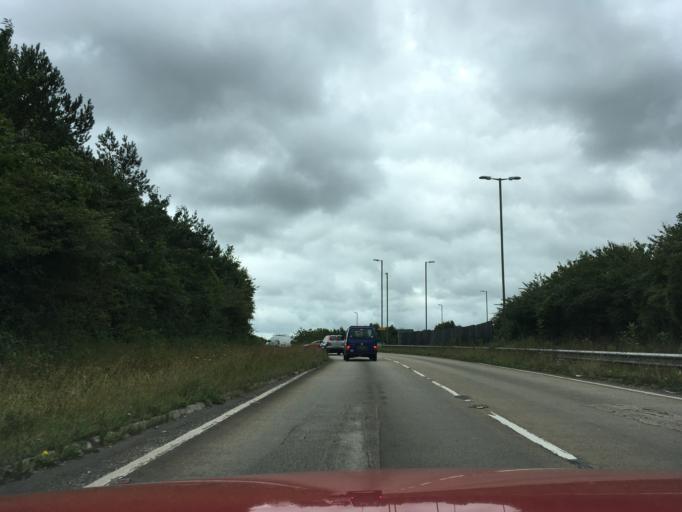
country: GB
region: England
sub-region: Devon
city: Marldon
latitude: 50.4578
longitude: -3.5908
